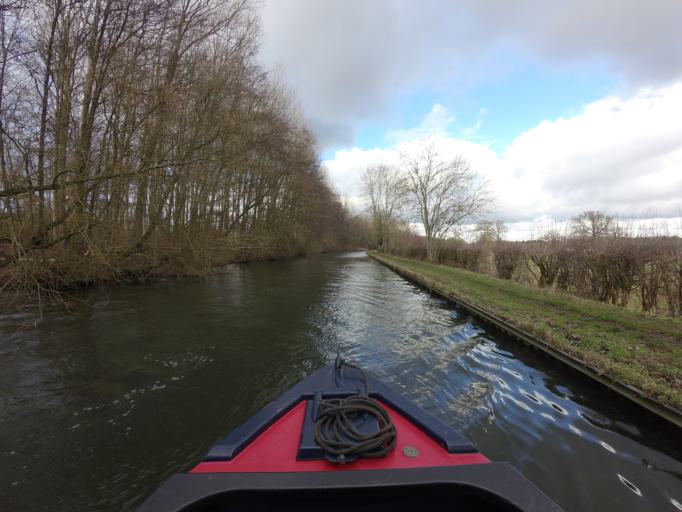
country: GB
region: England
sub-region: Northamptonshire
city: Long Buckby
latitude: 52.2530
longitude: -1.0842
